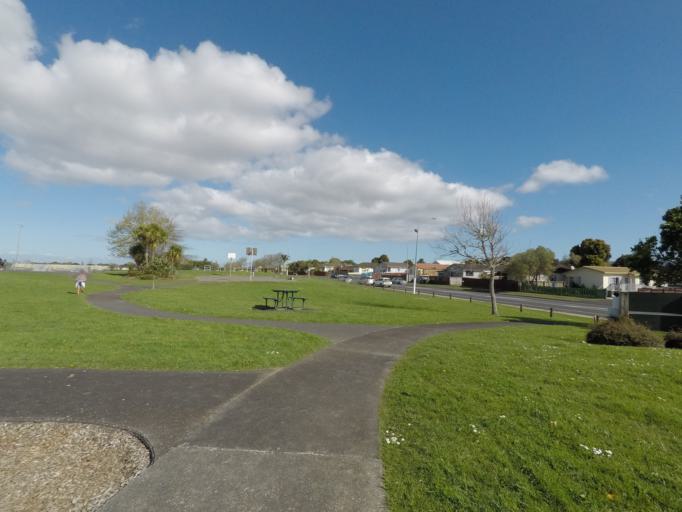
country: NZ
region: Auckland
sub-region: Auckland
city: Rosebank
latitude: -36.8596
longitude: 174.6033
